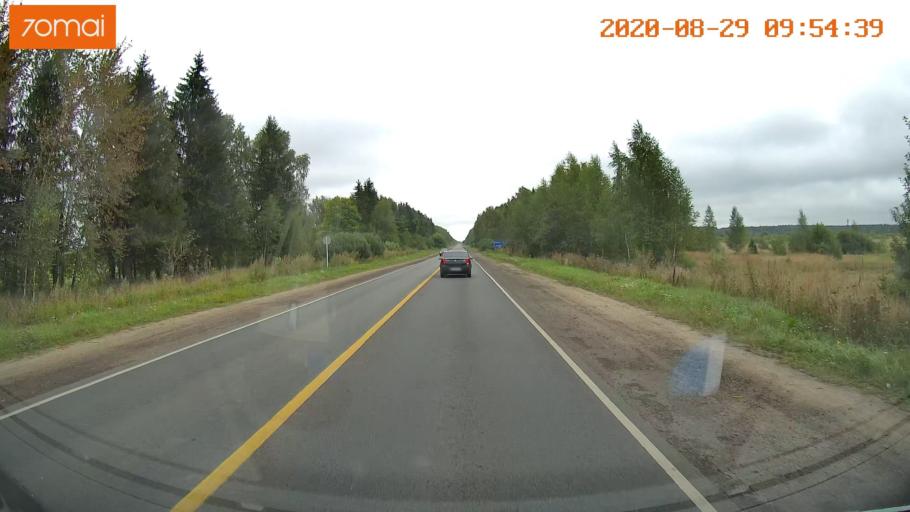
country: RU
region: Ivanovo
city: Zarechnyy
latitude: 57.4235
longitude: 42.2436
